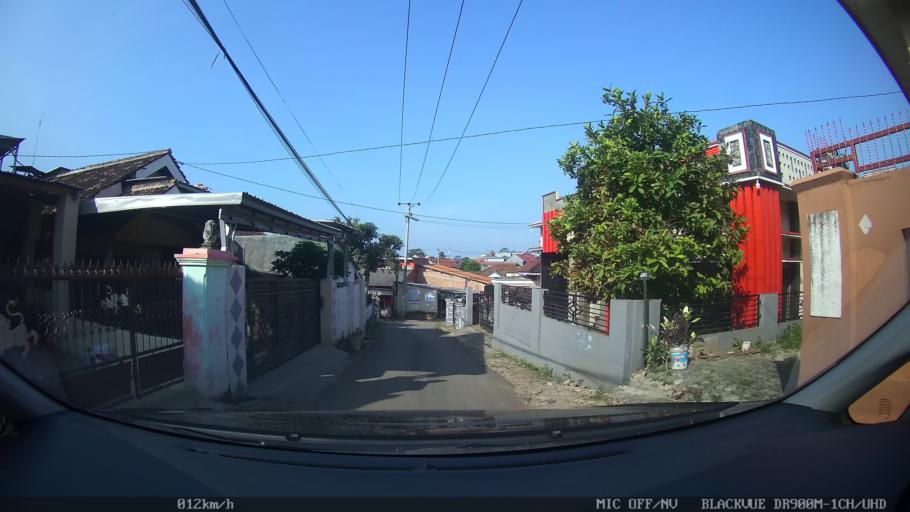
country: ID
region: Lampung
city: Kedaton
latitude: -5.3746
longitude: 105.2326
